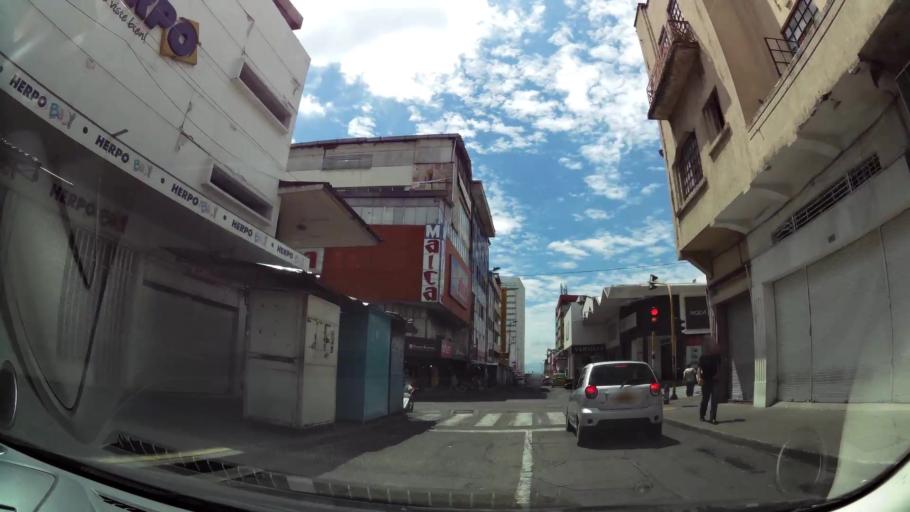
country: CO
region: Valle del Cauca
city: Cali
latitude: 3.4502
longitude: -76.5315
